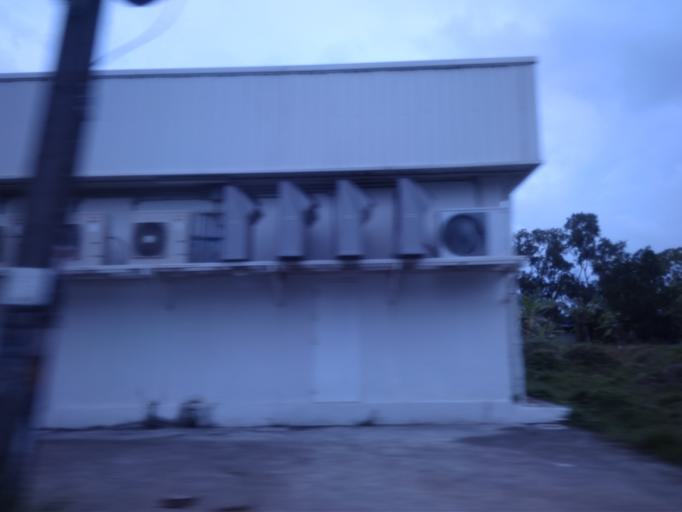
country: TH
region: Phuket
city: Mueang Phuket
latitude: 7.8420
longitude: 98.3766
